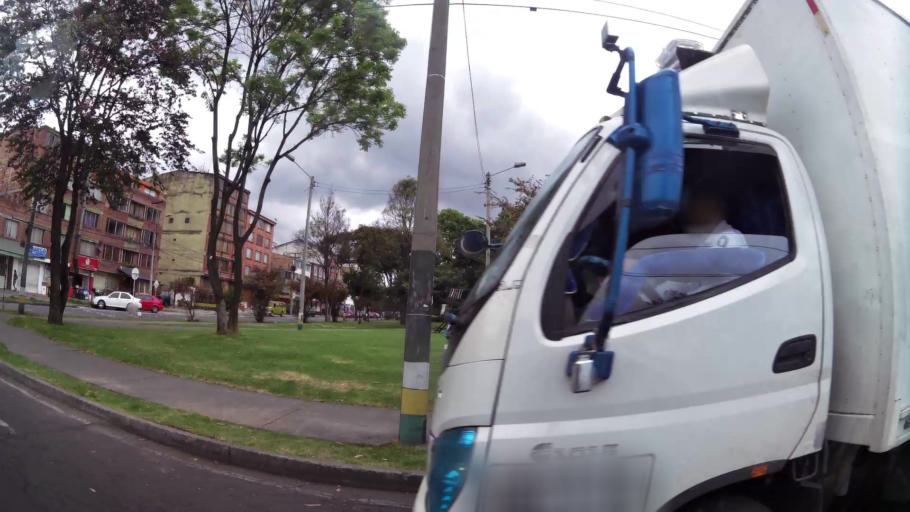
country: CO
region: Bogota D.C.
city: Bogota
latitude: 4.6062
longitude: -74.1024
